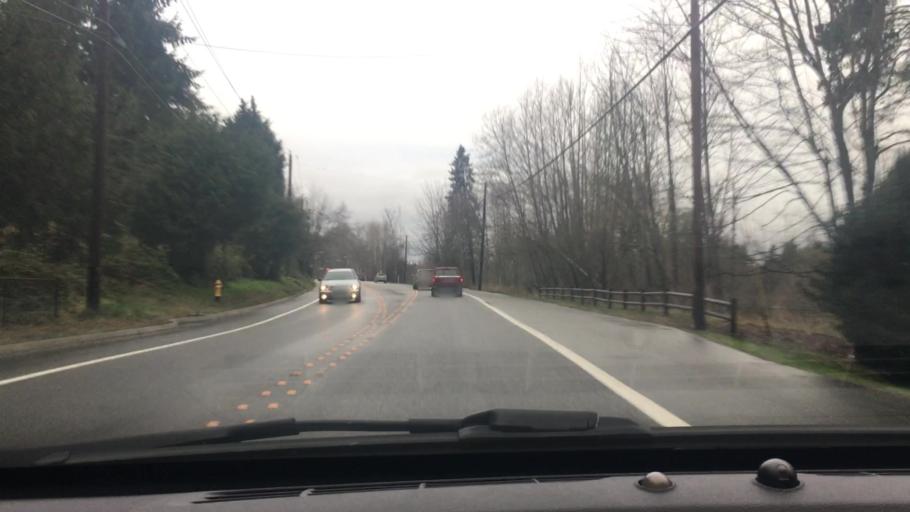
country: US
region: Washington
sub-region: King County
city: Redmond
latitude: 47.6547
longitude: -122.1180
